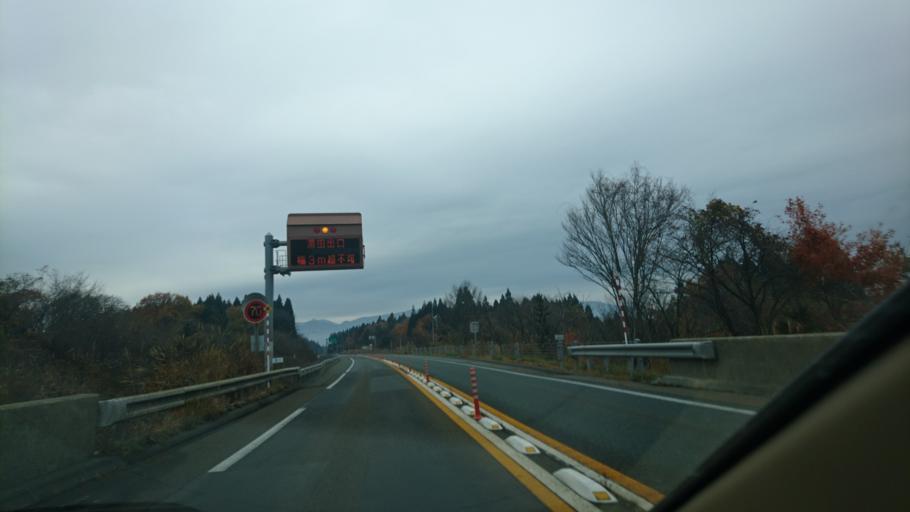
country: JP
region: Iwate
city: Kitakami
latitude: 39.2891
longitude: 140.9907
